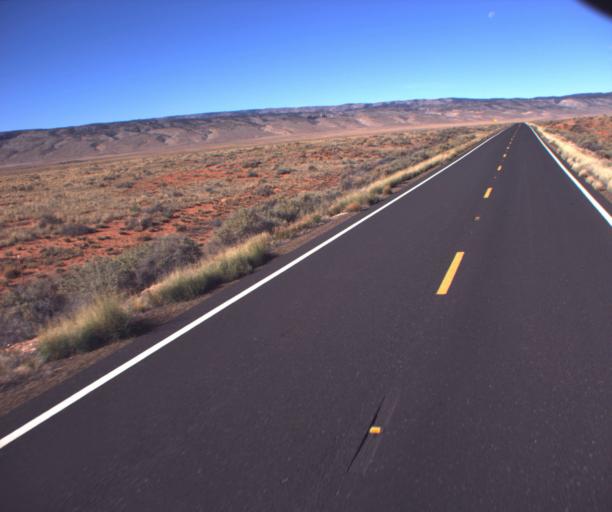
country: US
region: Arizona
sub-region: Coconino County
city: Page
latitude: 36.7118
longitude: -111.9768
